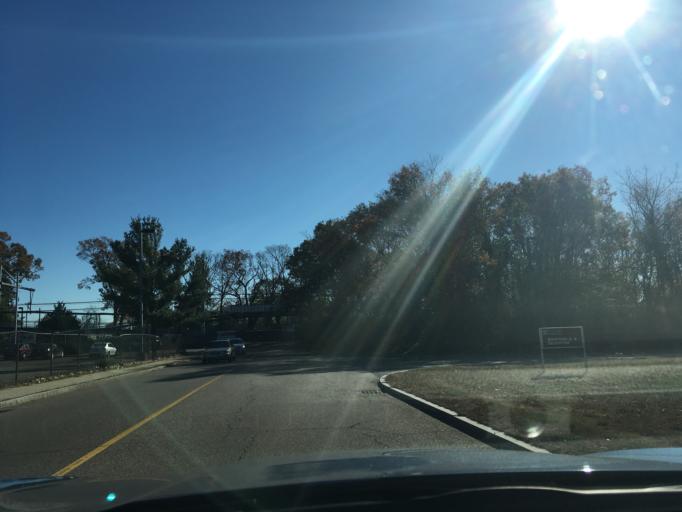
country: US
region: Massachusetts
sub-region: Bristol County
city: North Seekonk
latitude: 41.8985
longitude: -71.3565
